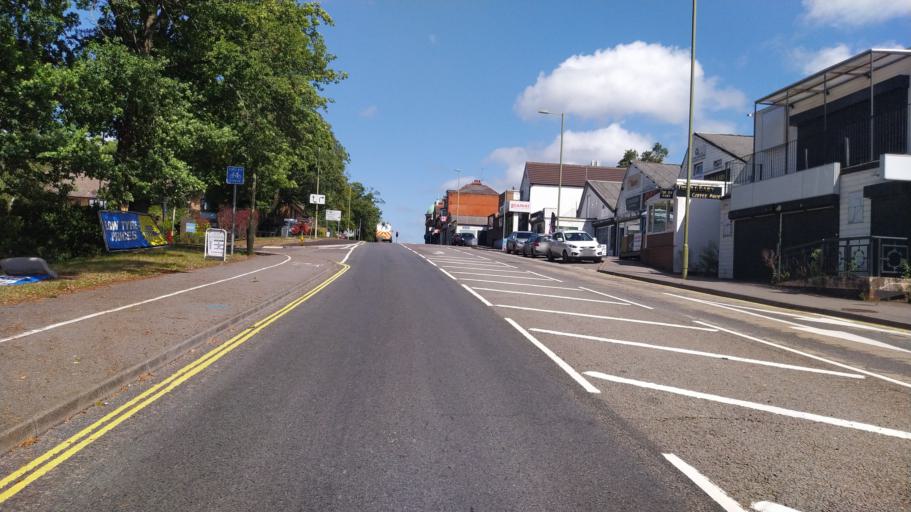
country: GB
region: England
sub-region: Hampshire
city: Bordon
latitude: 51.1105
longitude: -0.8642
